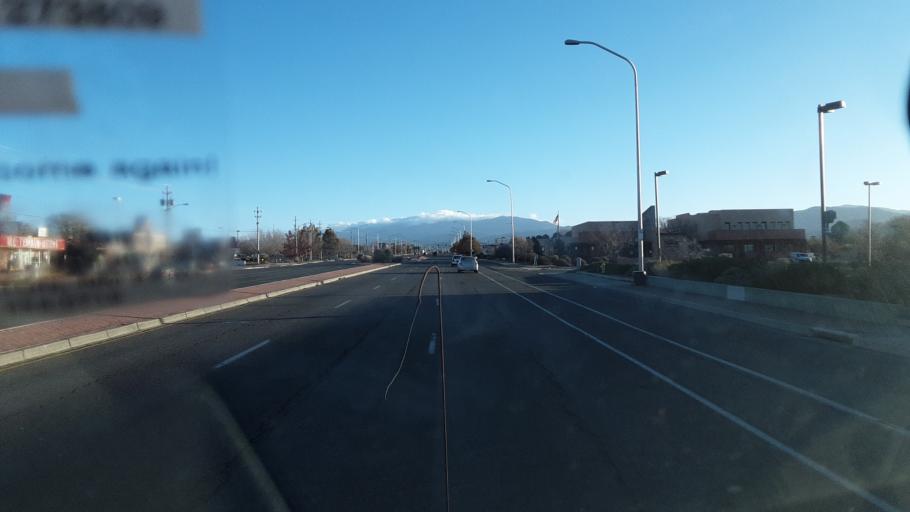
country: US
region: New Mexico
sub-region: Santa Fe County
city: Agua Fria
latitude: 35.6497
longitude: -106.0007
